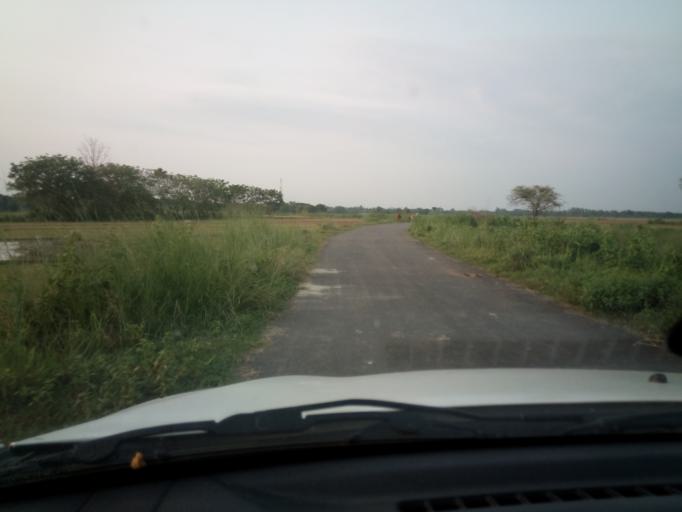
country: IN
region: Assam
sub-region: Udalguri
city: Udalguri
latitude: 26.6755
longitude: 92.1082
